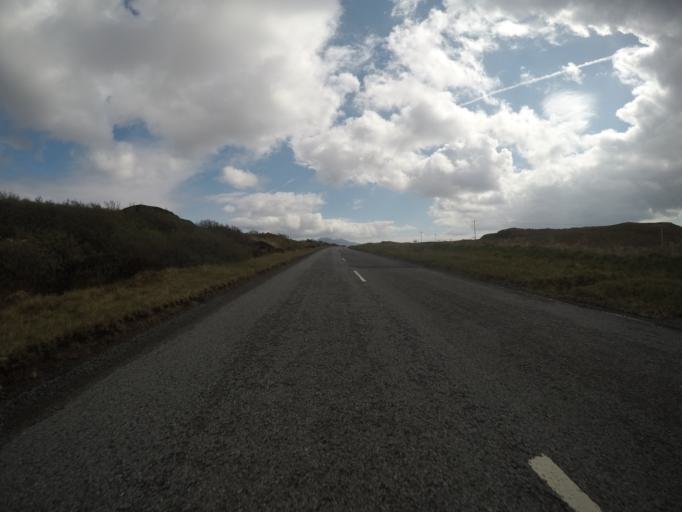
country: GB
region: Scotland
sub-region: Highland
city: Isle of Skye
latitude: 57.3184
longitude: -6.3225
